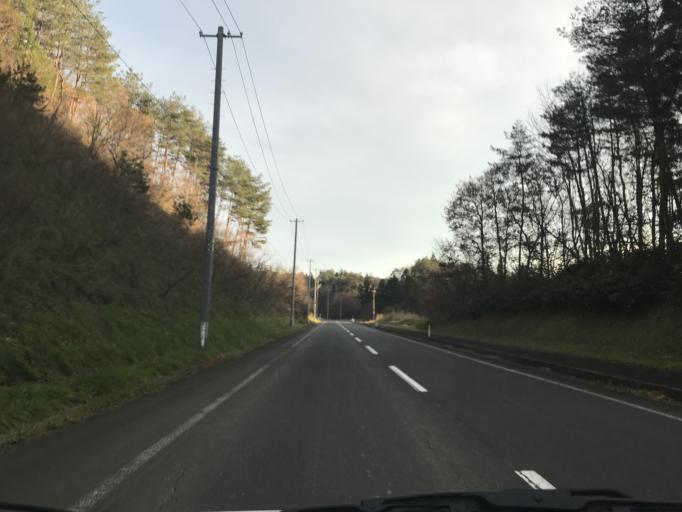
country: JP
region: Iwate
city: Ichinoseki
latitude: 38.9889
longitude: 141.0670
